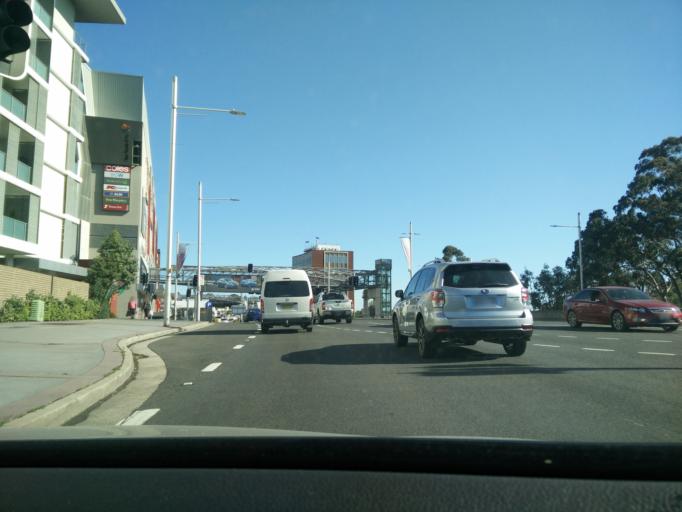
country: AU
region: New South Wales
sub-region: Ryde
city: Denistone
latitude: -33.8103
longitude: 151.1061
